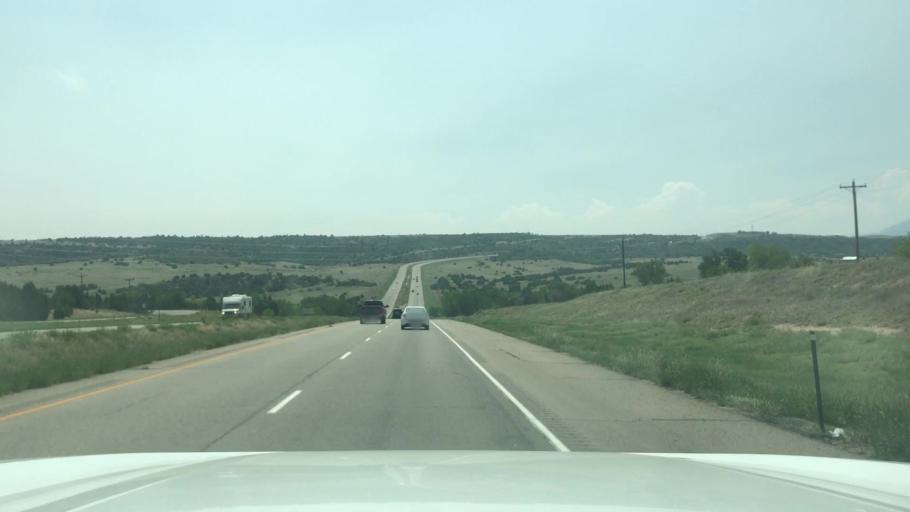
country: US
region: Colorado
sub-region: Pueblo County
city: Colorado City
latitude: 37.9538
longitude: -104.8014
